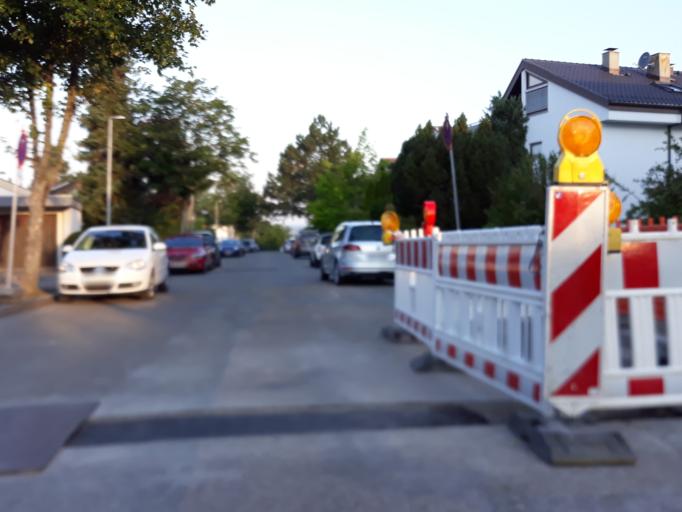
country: DE
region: Baden-Wuerttemberg
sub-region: Regierungsbezirk Stuttgart
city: Boeblingen
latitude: 48.6788
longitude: 9.0329
